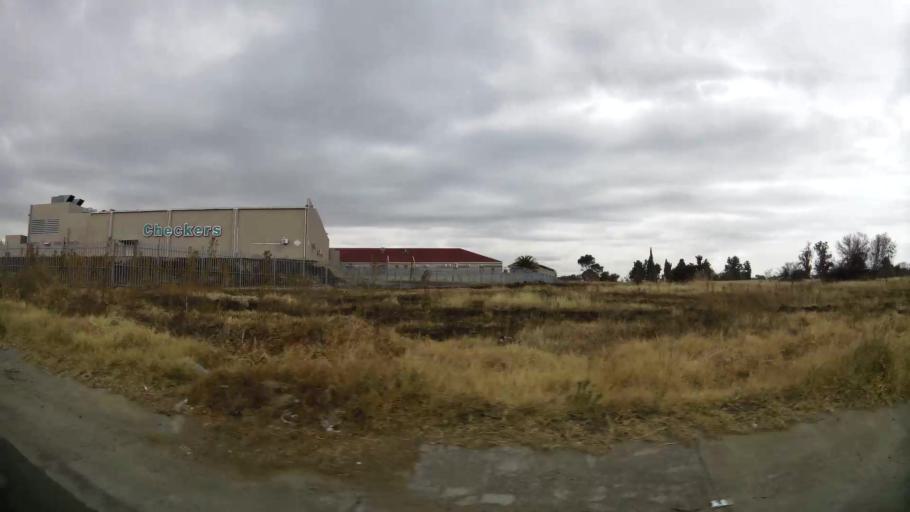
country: ZA
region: Orange Free State
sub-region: Fezile Dabi District Municipality
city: Kroonstad
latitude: -27.6491
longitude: 27.2282
